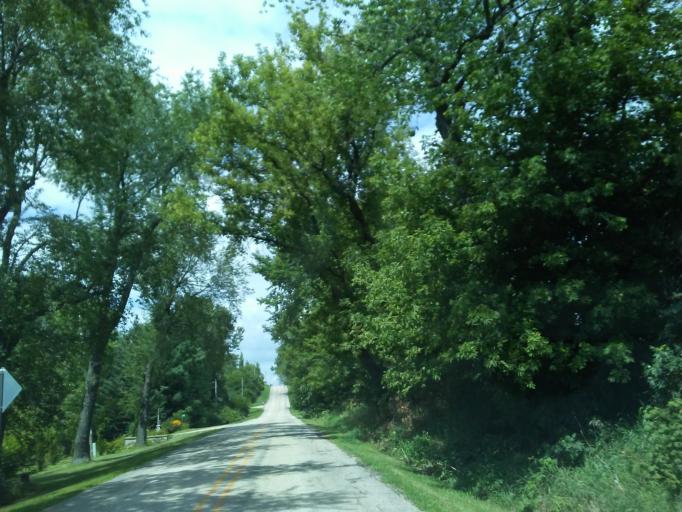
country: US
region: Wisconsin
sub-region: Dane County
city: Verona
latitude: 43.0021
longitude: -89.5782
